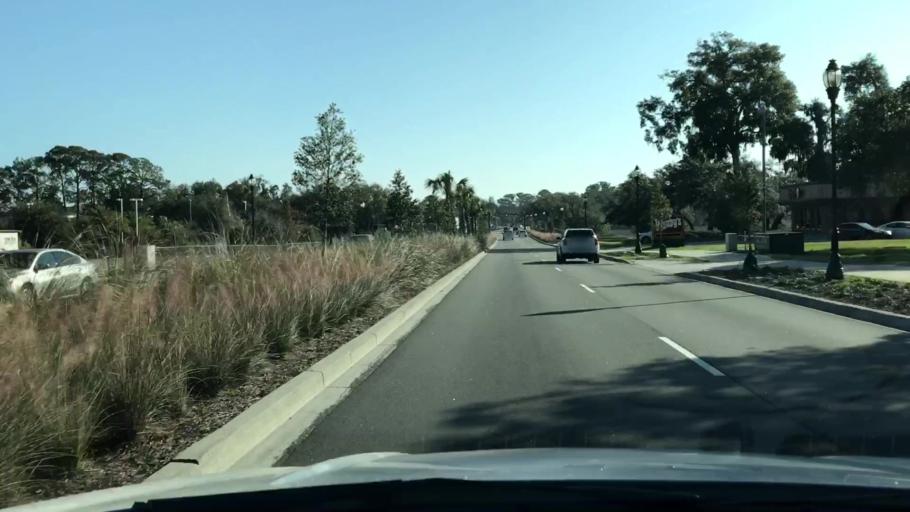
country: US
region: South Carolina
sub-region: Beaufort County
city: Burton
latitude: 32.4414
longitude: -80.6974
